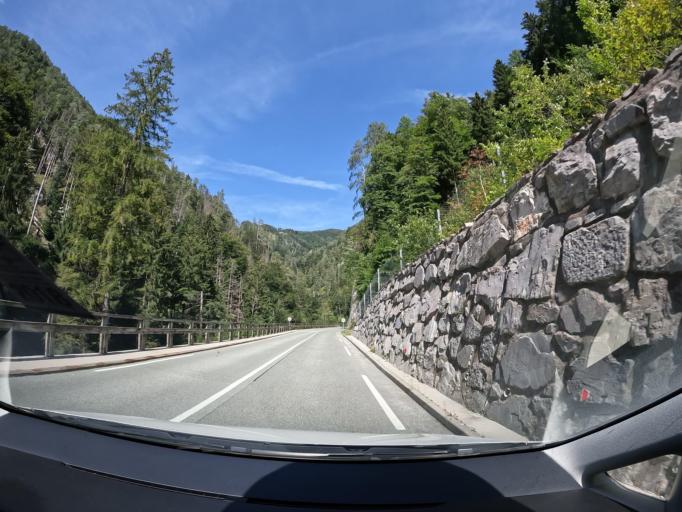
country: SI
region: Trzic
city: Trzic
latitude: 46.4166
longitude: 14.2941
